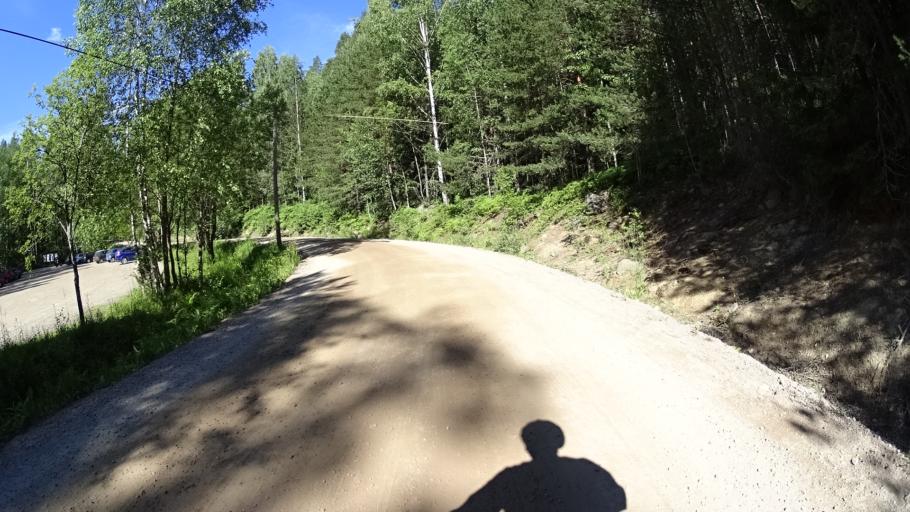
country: FI
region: Uusimaa
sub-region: Helsinki
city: Espoo
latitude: 60.3100
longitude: 24.5214
